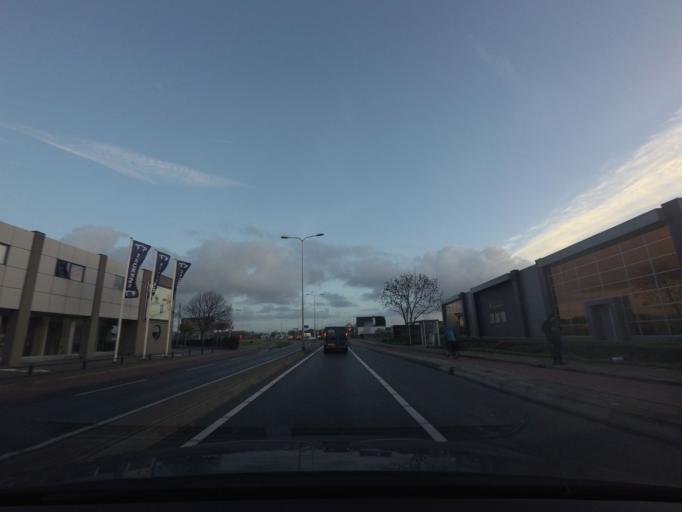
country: NL
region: South Holland
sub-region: Gemeente Lisse
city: Lisse
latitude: 52.2431
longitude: 4.5394
